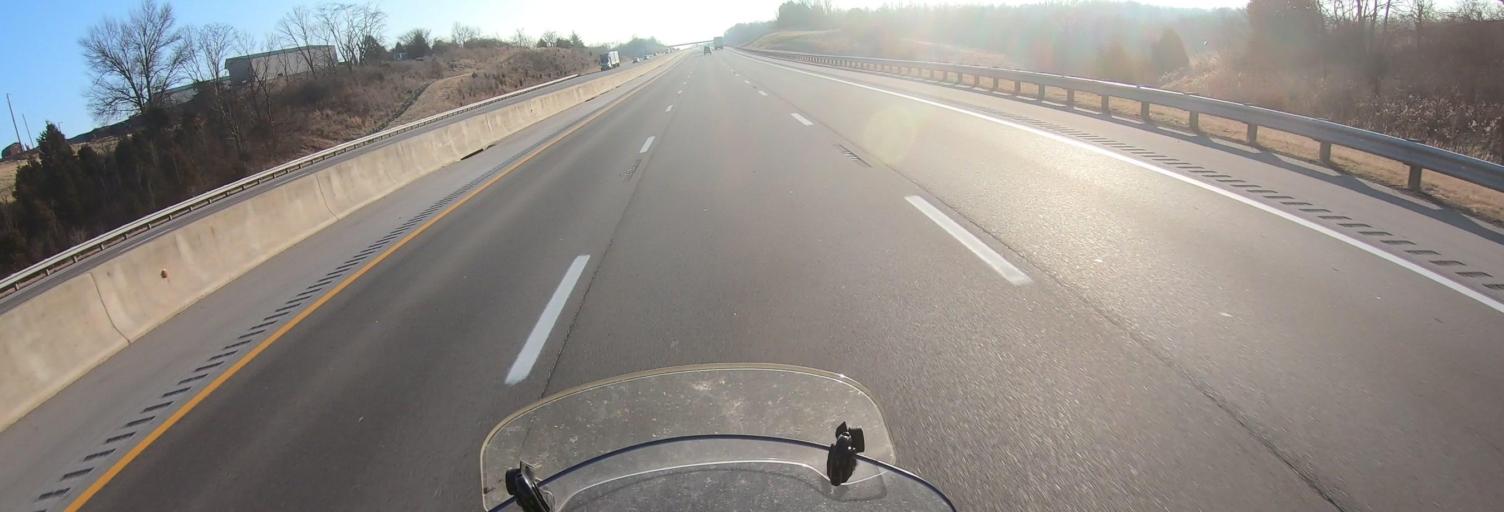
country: US
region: Kentucky
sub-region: Grant County
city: Williamstown
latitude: 38.6071
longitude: -84.5781
